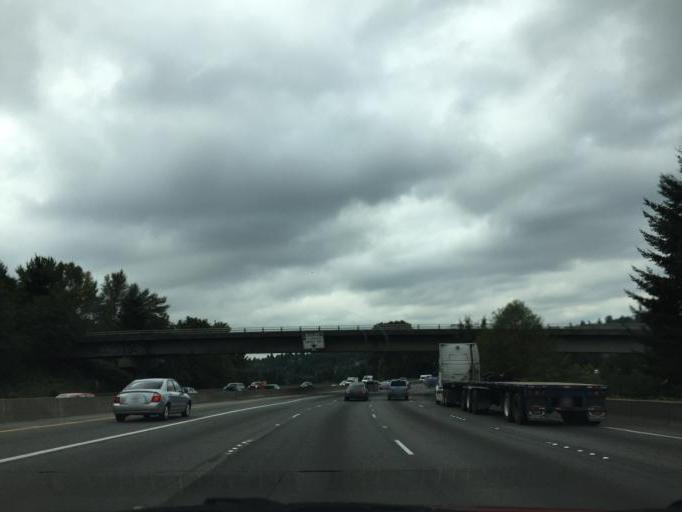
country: US
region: Washington
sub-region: King County
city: Tukwila
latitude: 47.4899
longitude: -122.2646
